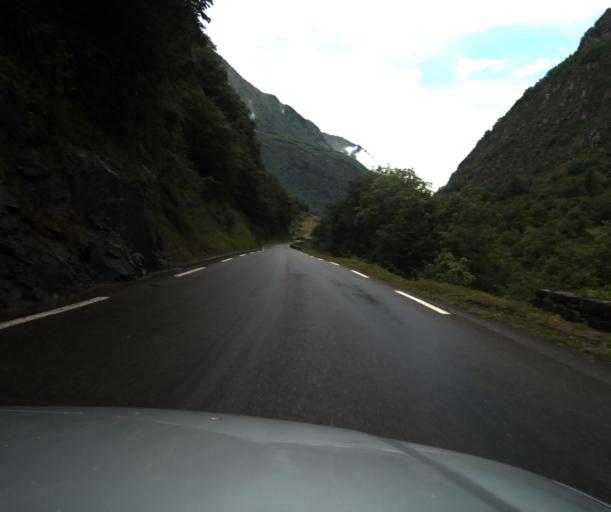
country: FR
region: Midi-Pyrenees
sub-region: Departement des Hautes-Pyrenees
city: Luz-Saint-Sauveur
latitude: 42.8315
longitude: 0.0029
